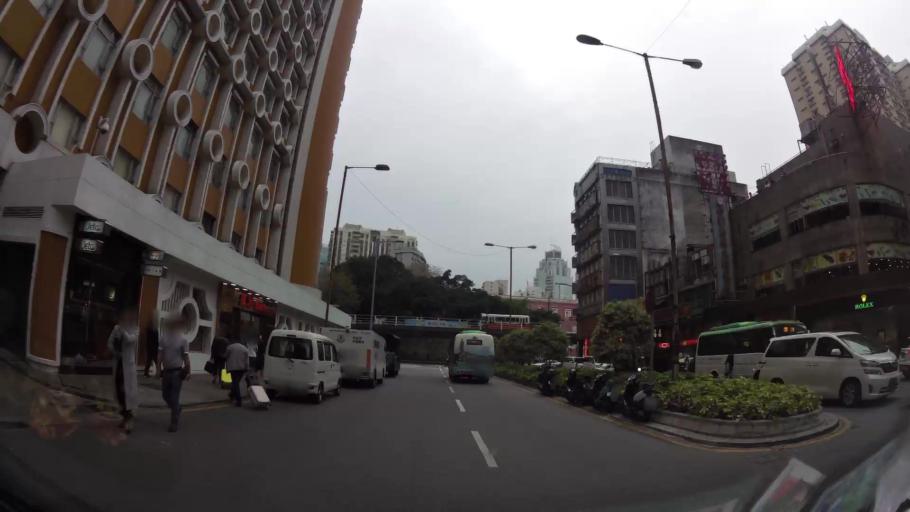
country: MO
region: Macau
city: Macau
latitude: 22.1903
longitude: 113.5453
